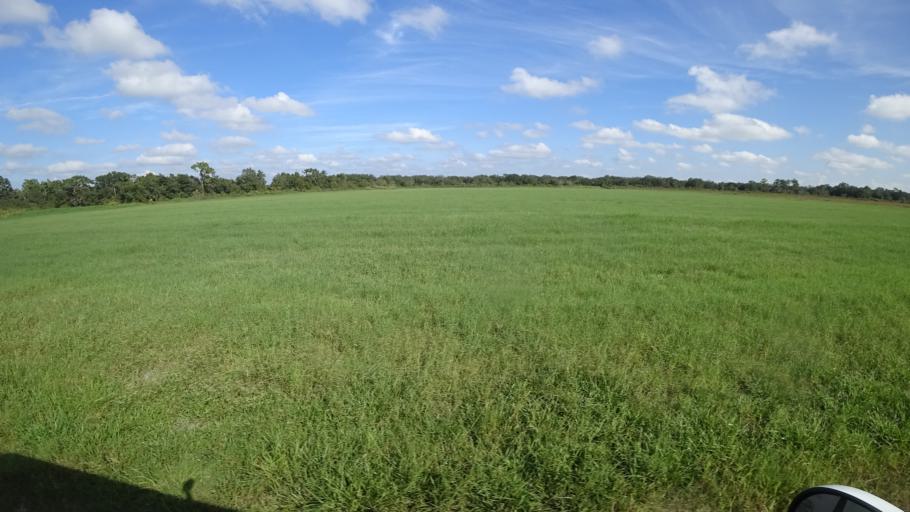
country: US
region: Florida
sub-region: Sarasota County
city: Lake Sarasota
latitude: 27.3714
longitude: -82.1574
